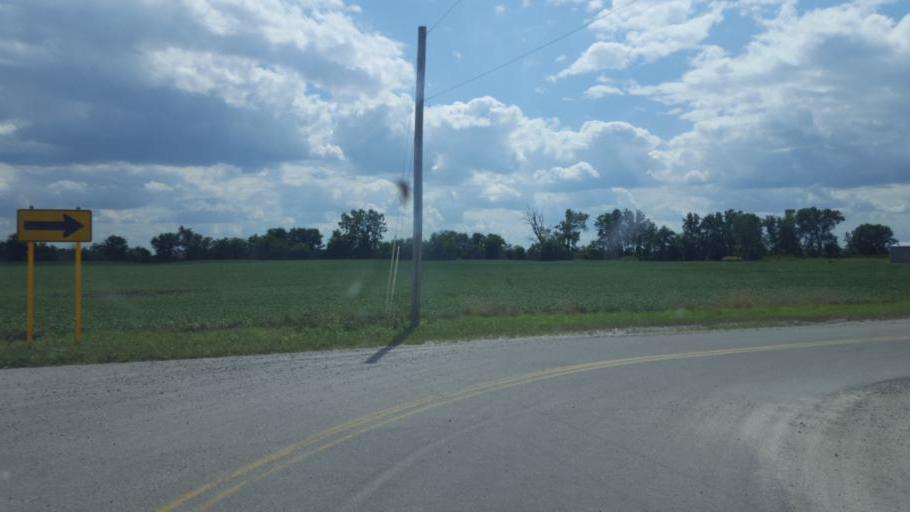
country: US
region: Ohio
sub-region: Lucas County
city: Curtice
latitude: 41.6556
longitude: -83.2577
